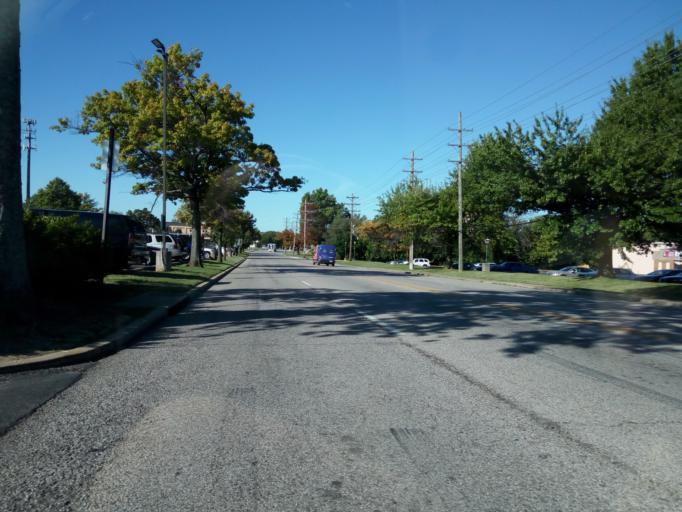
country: US
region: Kentucky
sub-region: Jefferson County
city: Audubon Park
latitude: 38.1931
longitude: -85.7403
